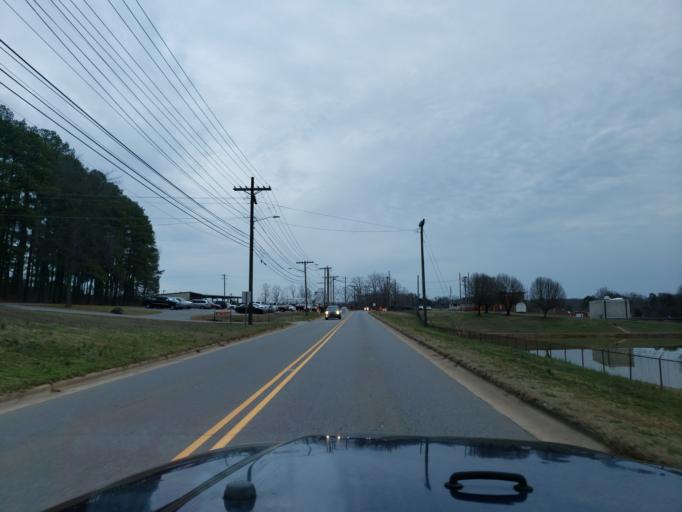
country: US
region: North Carolina
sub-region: Cleveland County
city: Shelby
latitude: 35.3042
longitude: -81.5591
